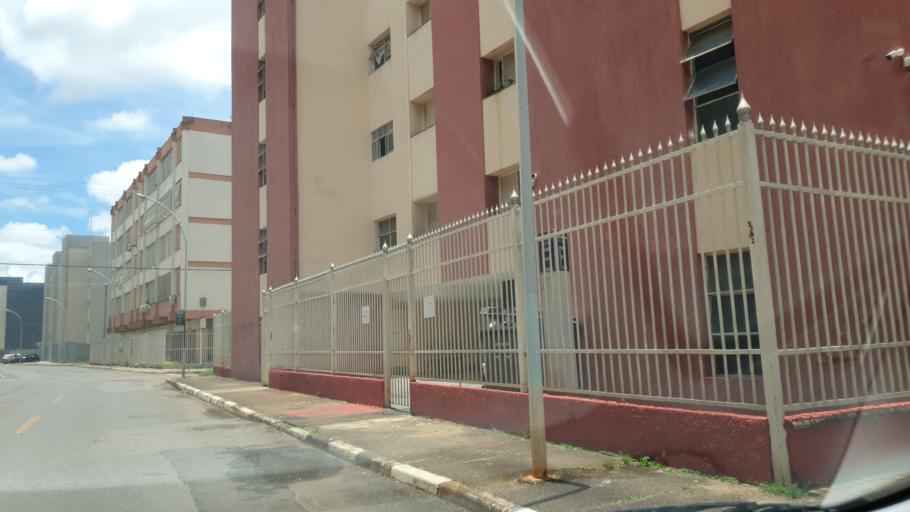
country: BR
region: Federal District
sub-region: Brasilia
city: Brasilia
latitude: -15.7950
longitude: -47.9366
